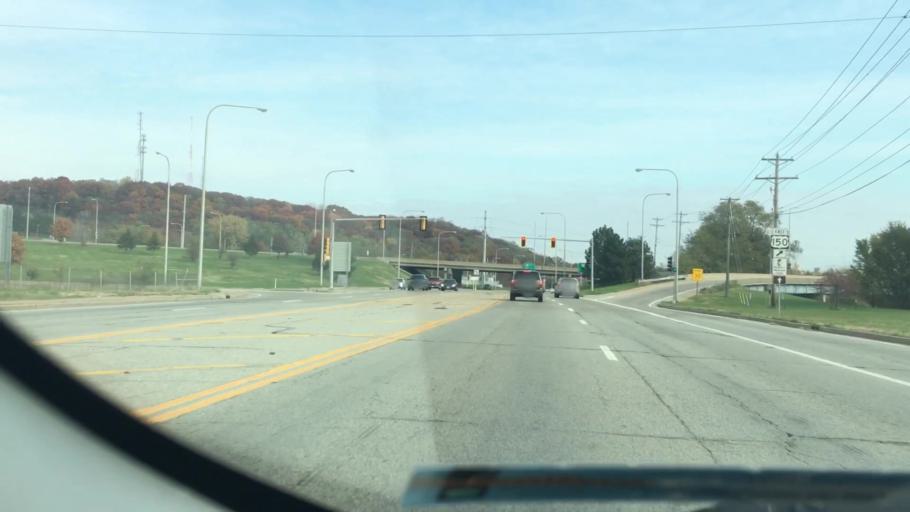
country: US
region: Illinois
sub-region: Peoria County
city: North Peoria
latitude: 40.7211
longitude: -89.5566
